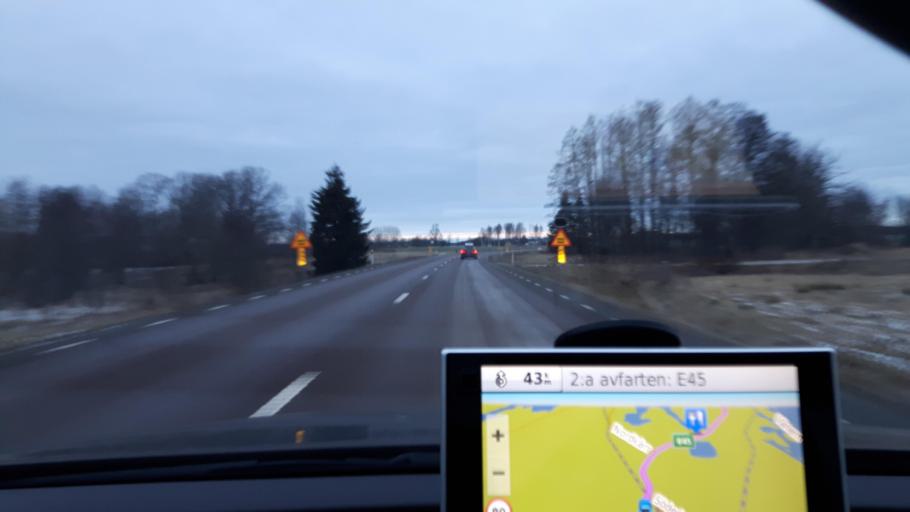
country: SE
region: Vaestra Goetaland
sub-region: Melleruds Kommun
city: Mellerud
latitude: 58.7165
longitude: 12.4559
